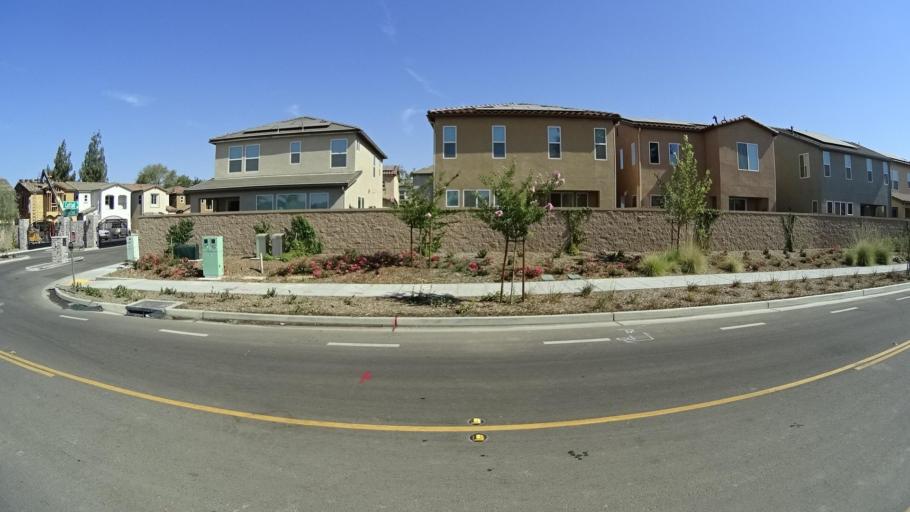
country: US
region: California
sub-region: Fresno County
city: Sunnyside
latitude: 36.7442
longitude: -119.6767
